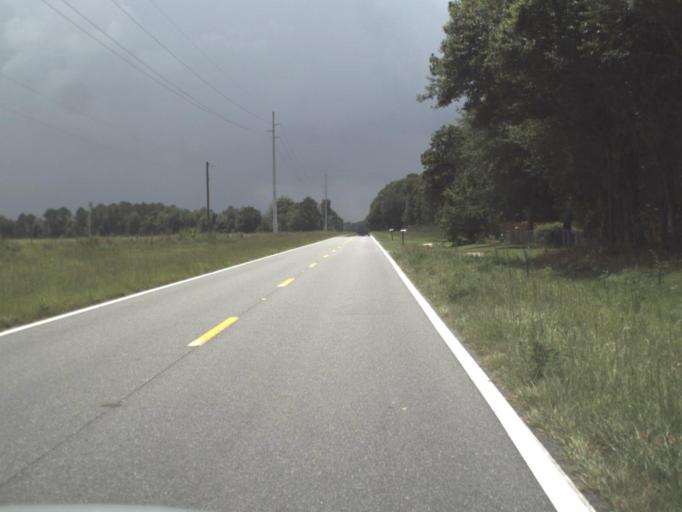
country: US
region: Florida
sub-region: Union County
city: Lake Butler
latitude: 29.9012
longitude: -82.3617
